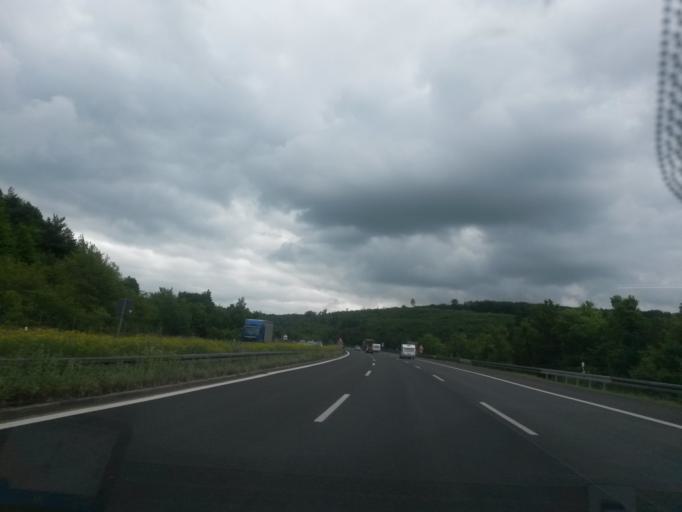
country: DE
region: Bavaria
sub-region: Regierungsbezirk Unterfranken
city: Fuchsstadt
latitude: 50.1141
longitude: 9.9575
